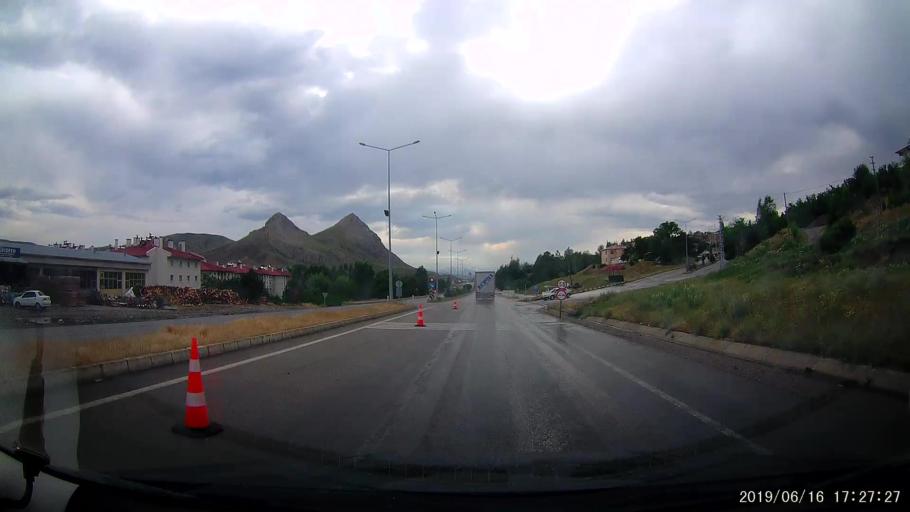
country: TR
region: Erzincan
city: Tercan
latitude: 39.7761
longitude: 40.3932
